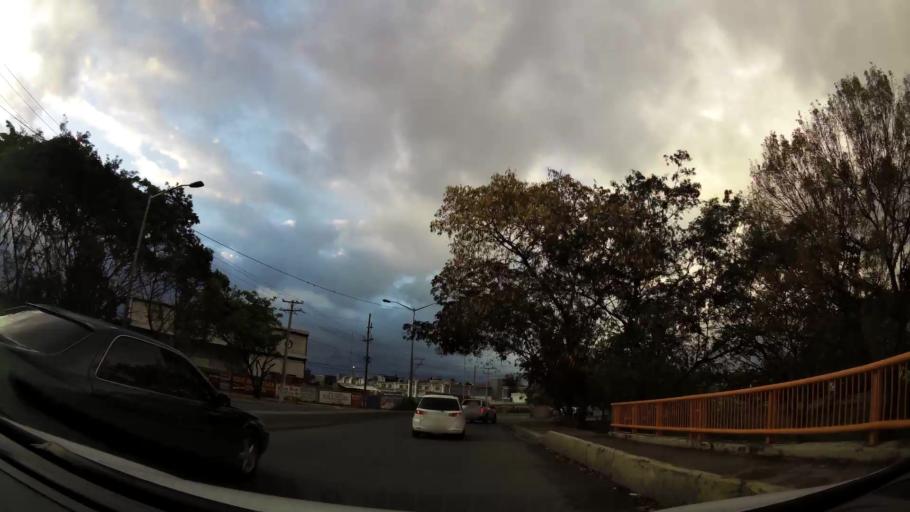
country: DO
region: Santo Domingo
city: Santo Domingo Oeste
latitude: 18.5048
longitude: -69.9992
